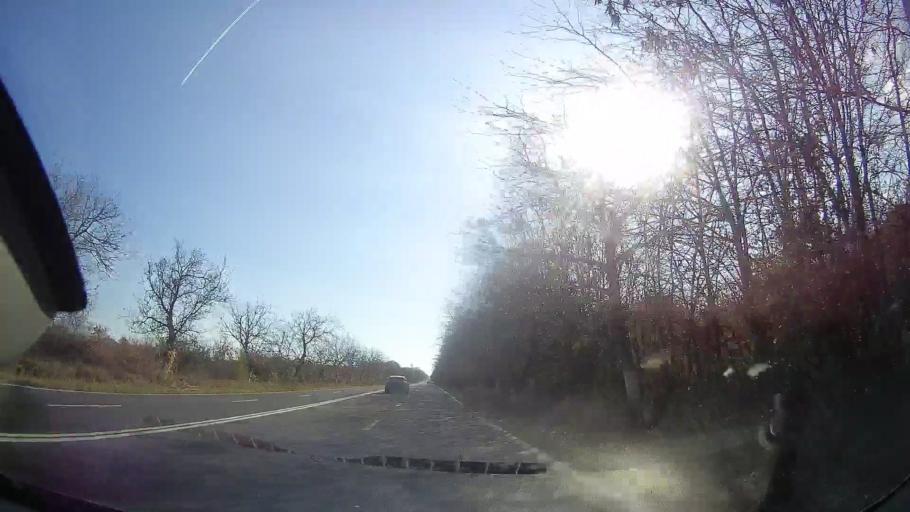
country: RO
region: Constanta
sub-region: Comuna Douazeci si Trei August
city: Dulcesti
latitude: 43.8812
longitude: 28.5734
